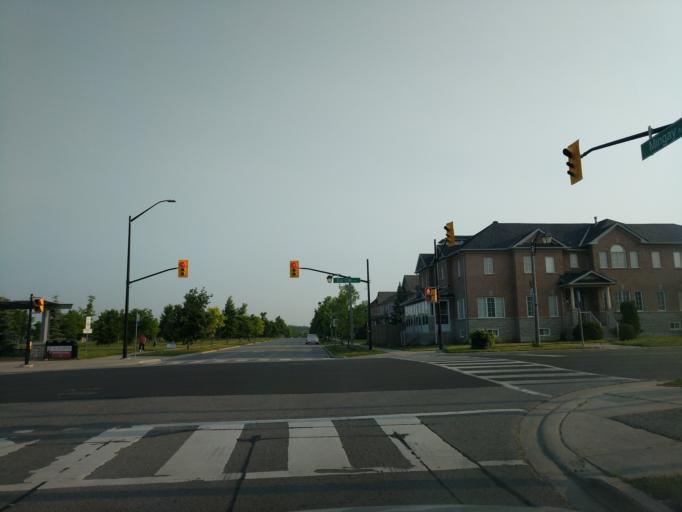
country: CA
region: Ontario
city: Markham
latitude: 43.8985
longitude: -79.2752
